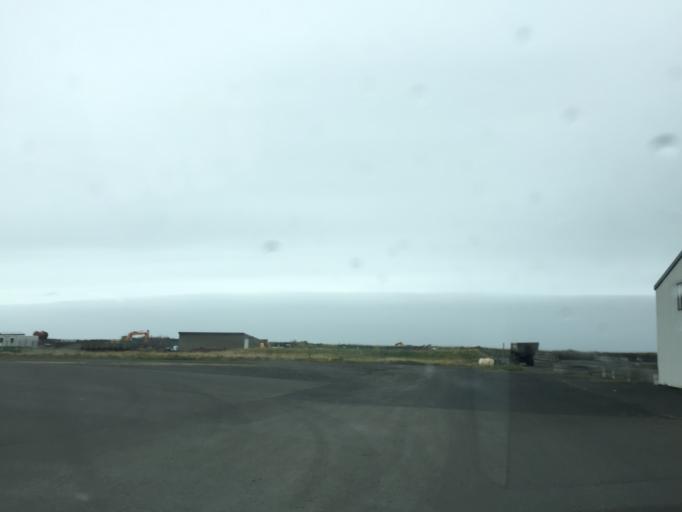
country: IS
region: South
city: Vestmannaeyjar
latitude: 63.4176
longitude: -18.9944
